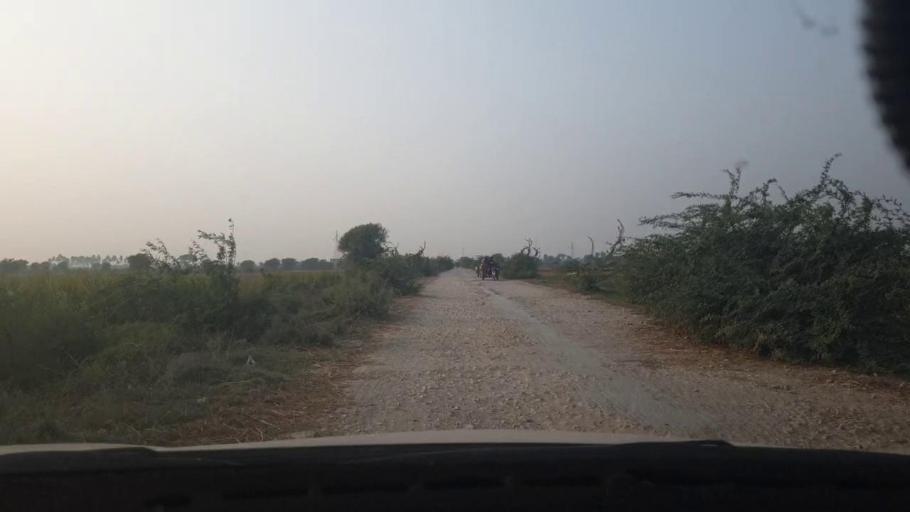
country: PK
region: Sindh
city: Bulri
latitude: 24.8508
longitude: 68.3439
